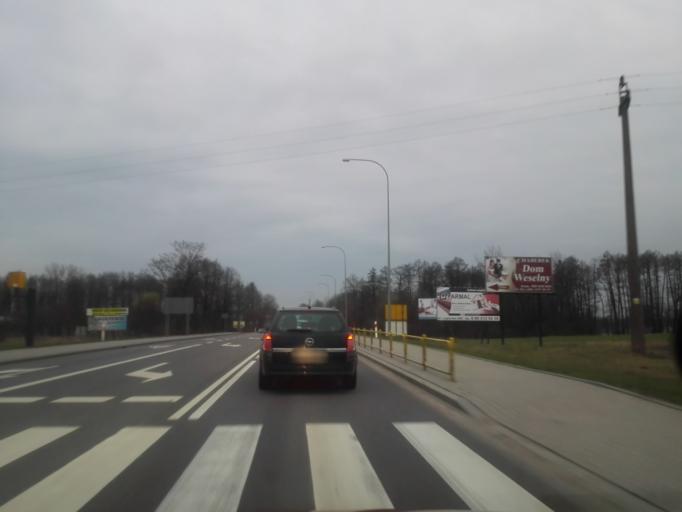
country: PL
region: Podlasie
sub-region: Powiat lomzynski
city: Piatnica
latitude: 53.2288
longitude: 22.1113
